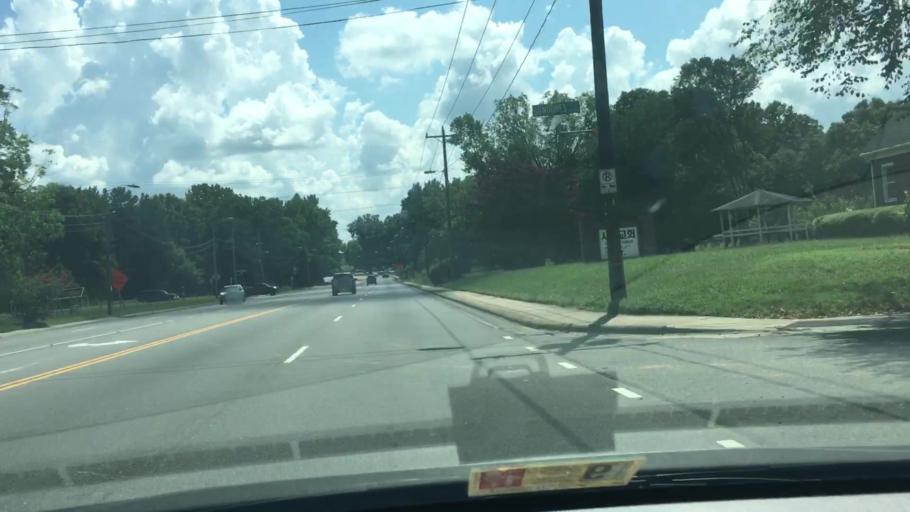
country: US
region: North Carolina
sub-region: Mecklenburg County
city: Charlotte
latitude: 35.2635
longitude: -80.7952
